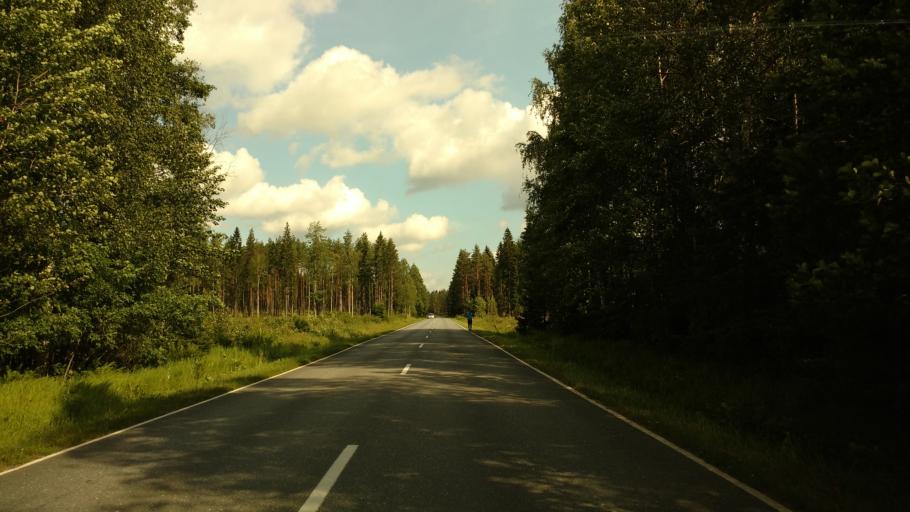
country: FI
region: Varsinais-Suomi
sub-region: Loimaa
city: Koski Tl
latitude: 60.6079
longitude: 23.1219
